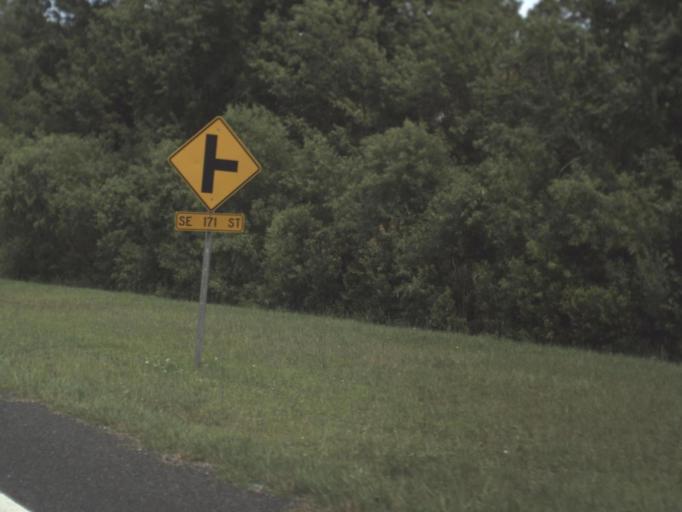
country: US
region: Florida
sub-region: Alachua County
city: Hawthorne
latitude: 29.6000
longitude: -82.1368
